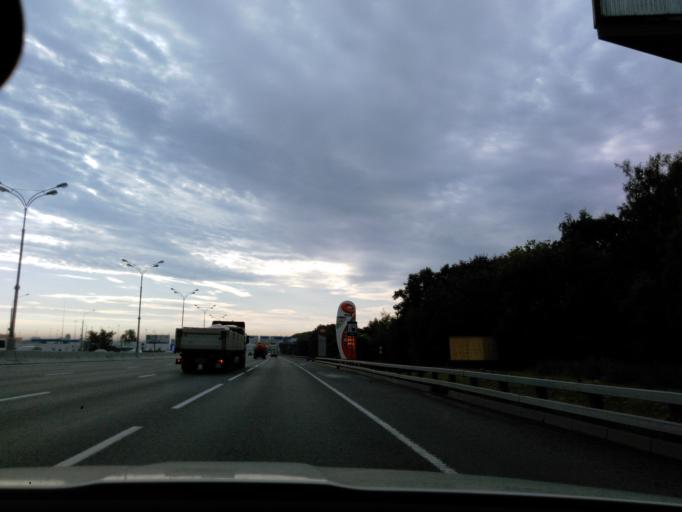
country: RU
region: Moscow
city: Vatutino
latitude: 55.8957
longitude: 37.6582
